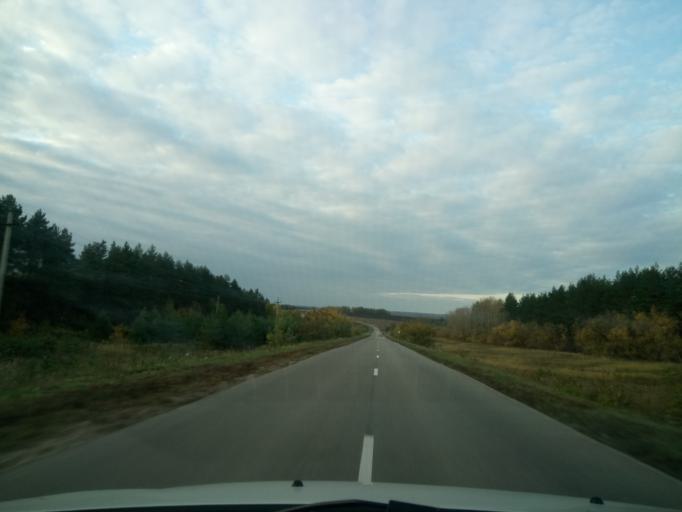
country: RU
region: Nizjnij Novgorod
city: Buturlino
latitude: 55.5313
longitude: 44.9924
